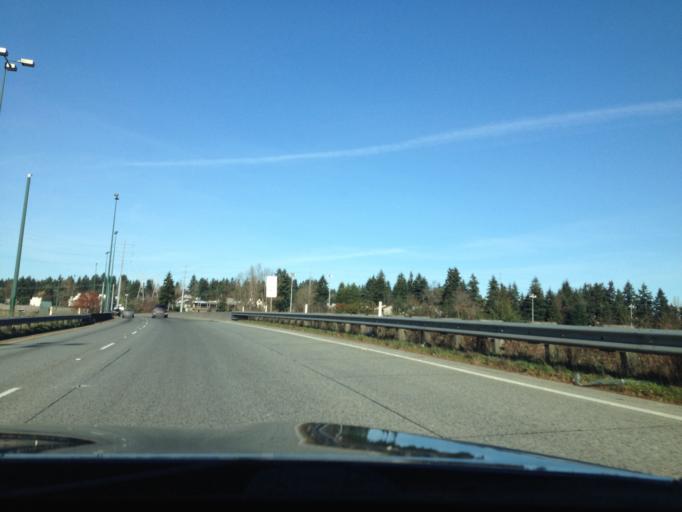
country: US
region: Washington
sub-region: King County
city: Newport
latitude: 47.5787
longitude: -122.1741
